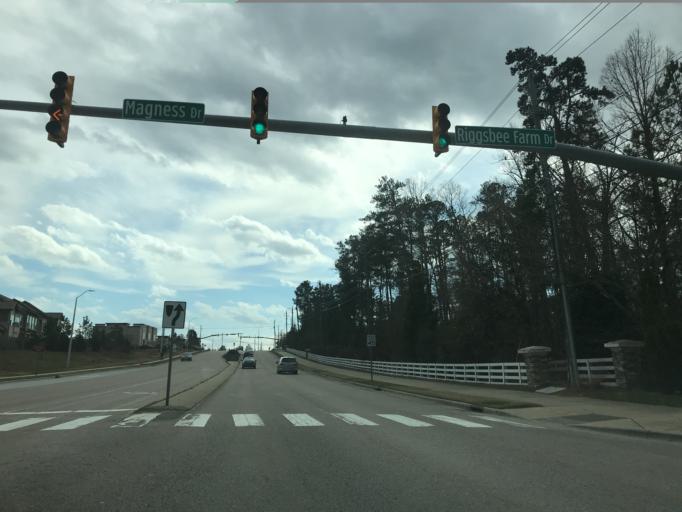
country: US
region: North Carolina
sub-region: Wake County
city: Morrisville
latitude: 35.7962
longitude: -78.8482
